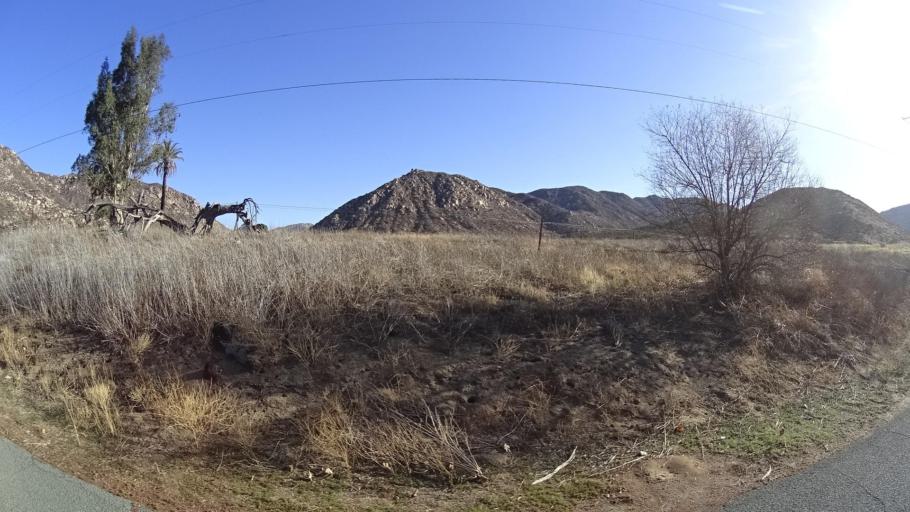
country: MX
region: Baja California
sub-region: Tecate
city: Lomas de Santa Anita
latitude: 32.6096
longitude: -116.6972
